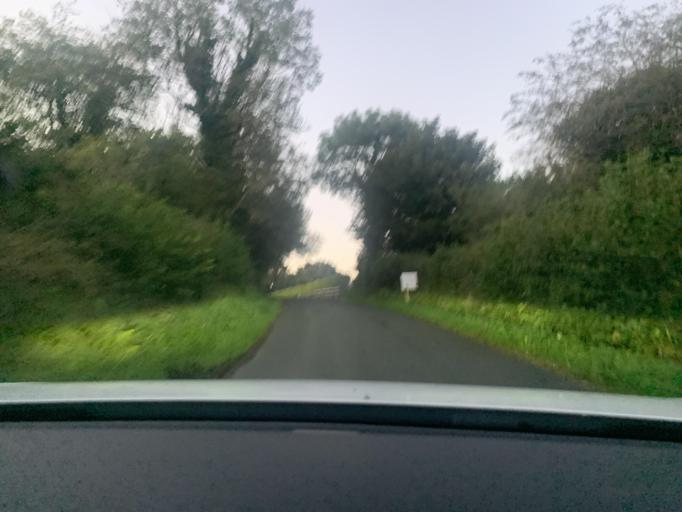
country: IE
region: Connaught
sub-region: County Leitrim
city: Manorhamilton
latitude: 54.2720
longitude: -8.2838
